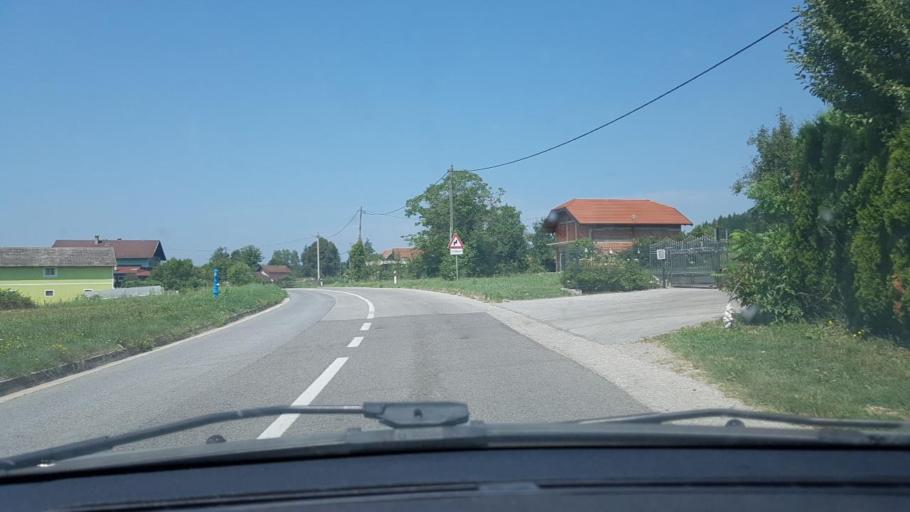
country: BA
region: Federation of Bosnia and Herzegovina
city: Velika Kladusa
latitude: 45.2155
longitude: 15.7595
